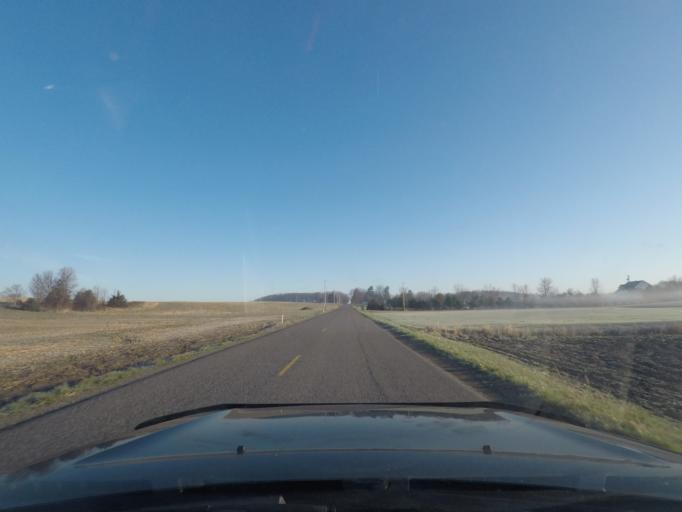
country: US
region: Indiana
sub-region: Elkhart County
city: Dunlap
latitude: 41.5909
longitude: -85.9253
